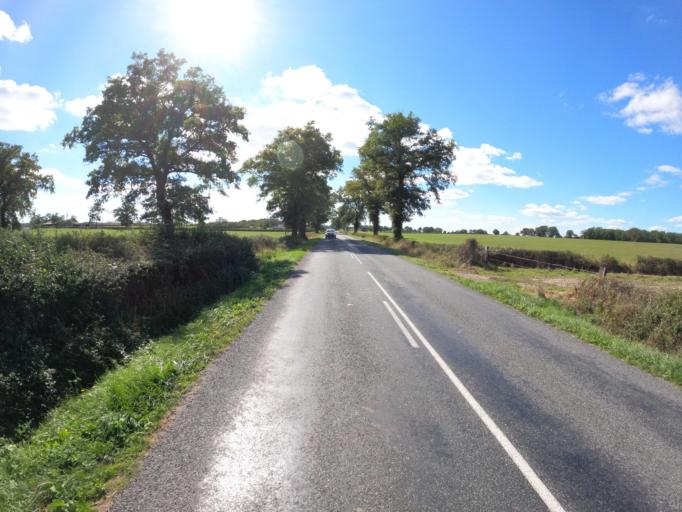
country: FR
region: Auvergne
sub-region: Departement de l'Allier
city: Doyet
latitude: 46.3893
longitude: 2.8040
